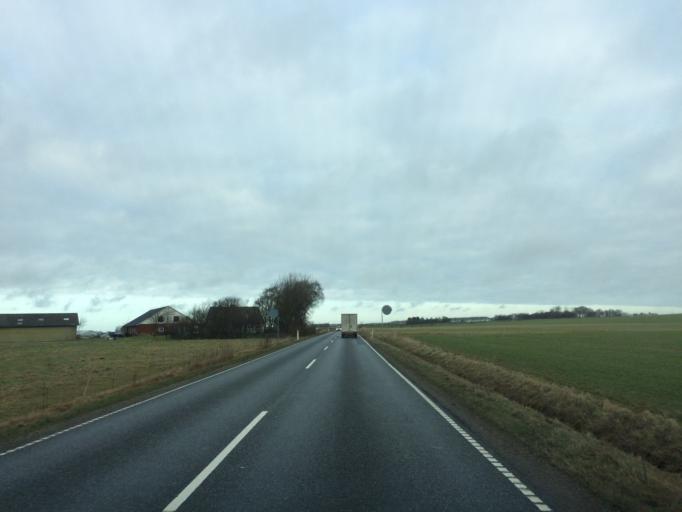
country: DK
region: Central Jutland
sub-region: Struer Kommune
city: Struer
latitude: 56.4328
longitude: 8.5181
